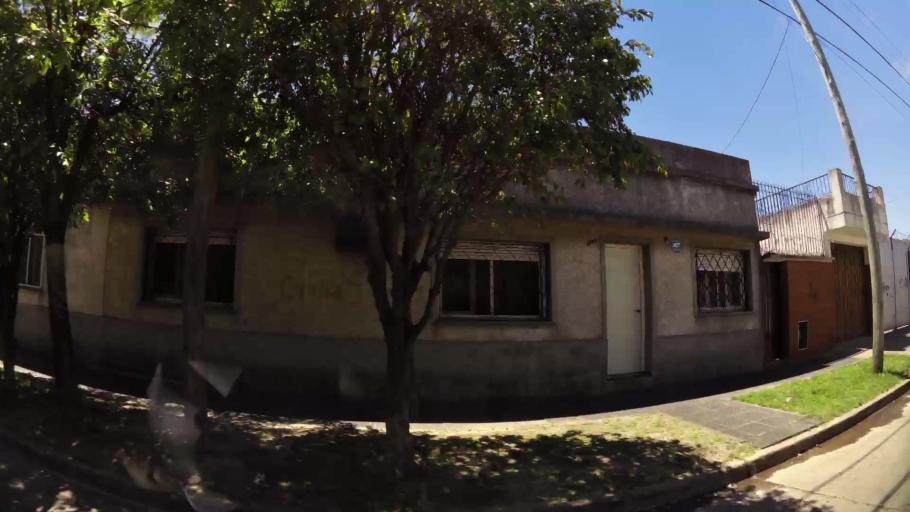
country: AR
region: Buenos Aires
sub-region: Partido de Quilmes
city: Quilmes
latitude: -34.7199
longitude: -58.3125
